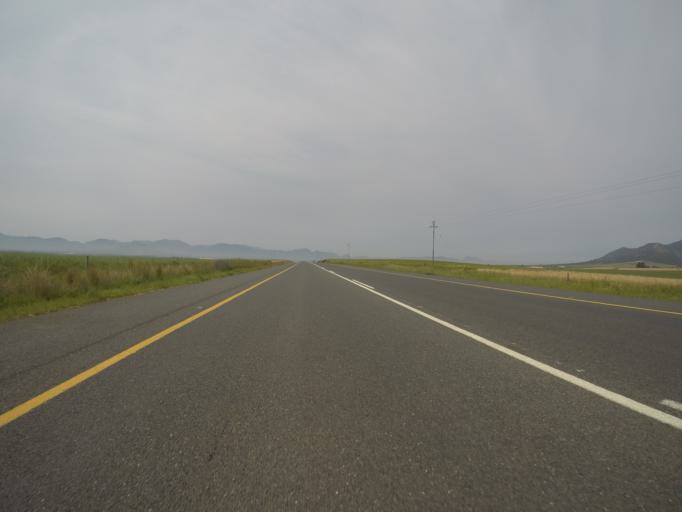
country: ZA
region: Western Cape
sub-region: West Coast District Municipality
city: Malmesbury
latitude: -33.5431
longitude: 18.8611
